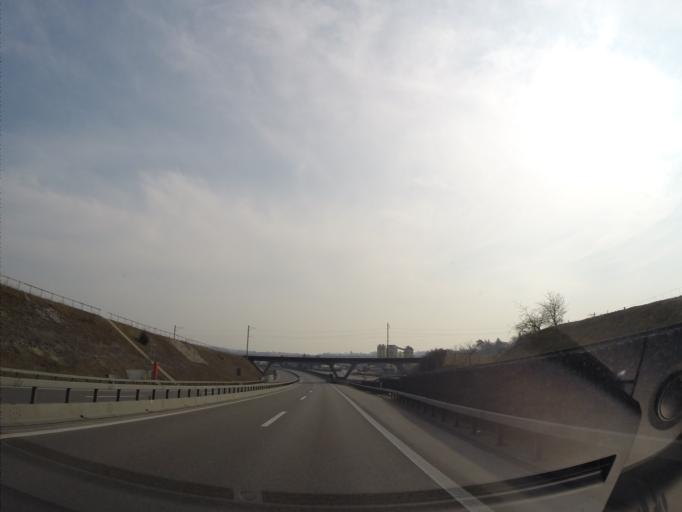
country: CH
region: Zurich
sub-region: Bezirk Andelfingen
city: Kleinandelfingen
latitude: 47.6102
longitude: 8.6863
